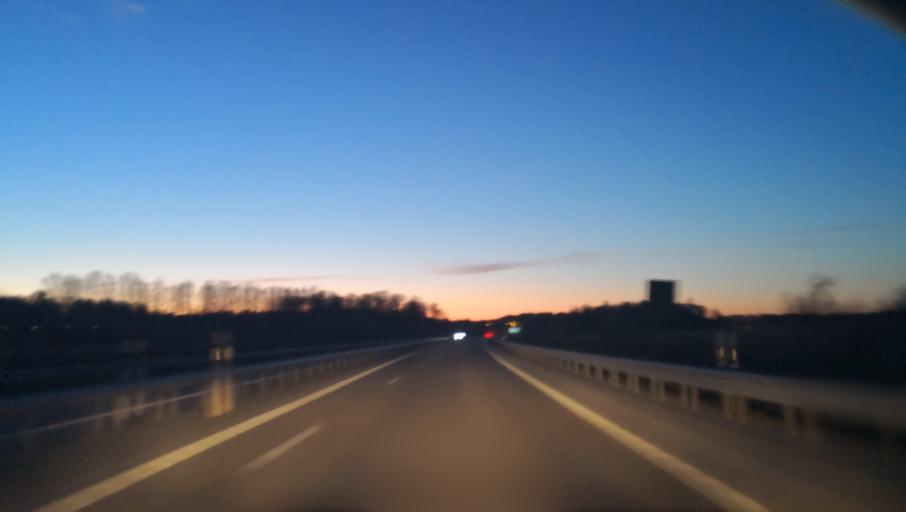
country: SE
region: Stockholm
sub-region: Nynashamns Kommun
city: Nynashamn
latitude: 58.9357
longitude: 17.9219
